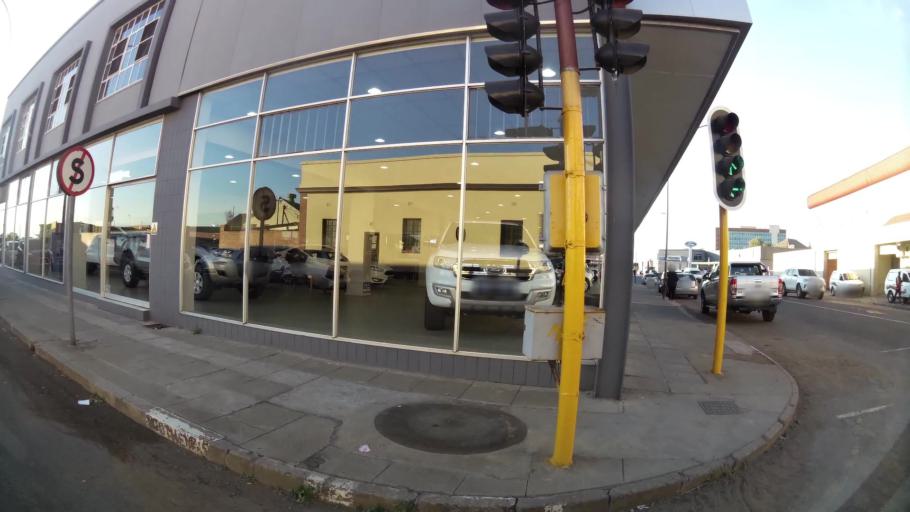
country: ZA
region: Northern Cape
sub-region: Frances Baard District Municipality
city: Kimberley
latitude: -28.7375
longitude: 24.7622
